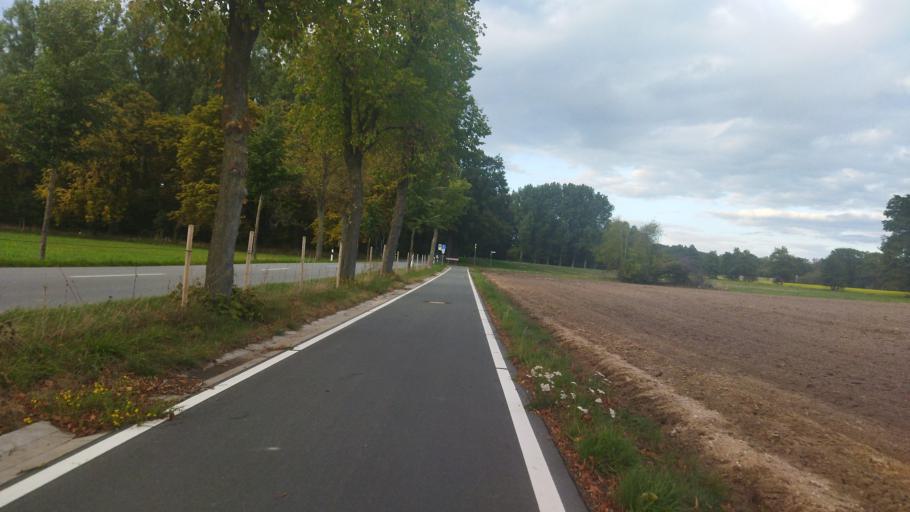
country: DE
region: North Rhine-Westphalia
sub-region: Regierungsbezirk Munster
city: Billerbeck
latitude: 51.9846
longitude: 7.2336
